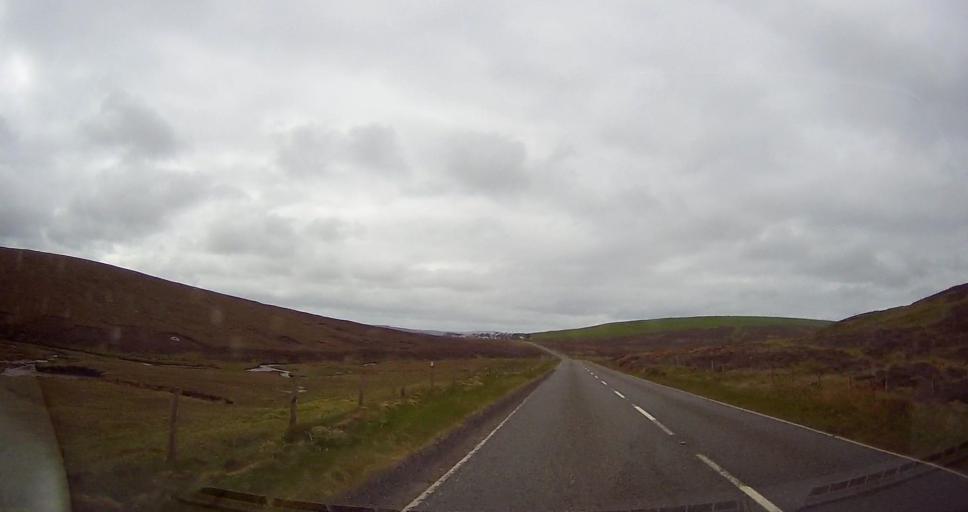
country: GB
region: Scotland
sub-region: Shetland Islands
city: Lerwick
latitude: 60.2508
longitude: -1.3815
